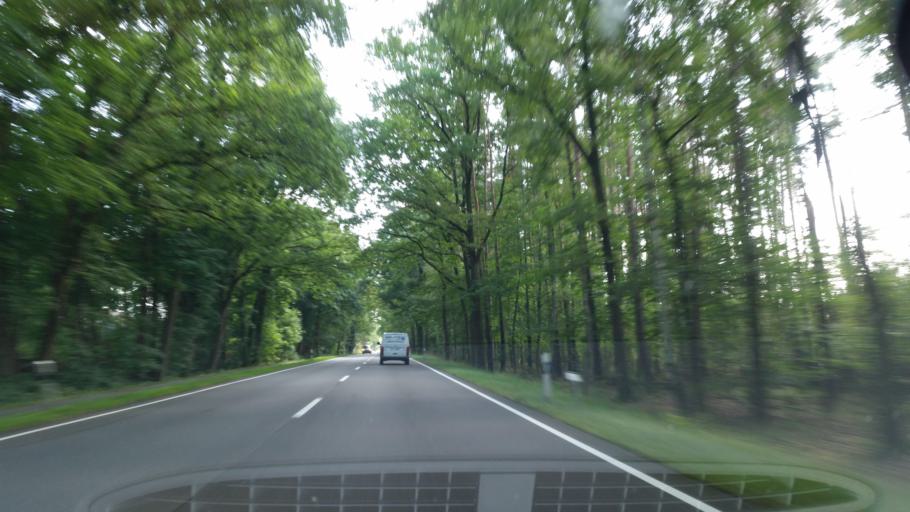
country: DE
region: Lower Saxony
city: Celle
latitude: 52.6590
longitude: 10.0531
